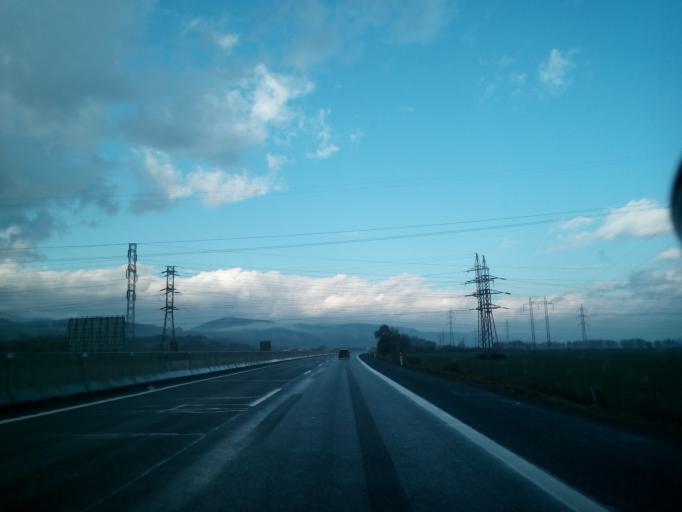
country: SK
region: Presovsky
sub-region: Okres Presov
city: Presov
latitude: 48.8632
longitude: 21.2614
